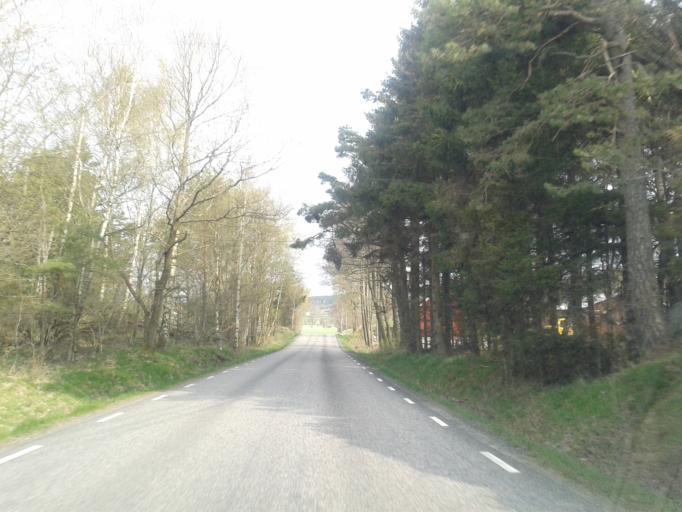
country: SE
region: Vaestra Goetaland
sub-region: Kungalvs Kommun
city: Kode
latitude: 57.9049
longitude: 11.8048
